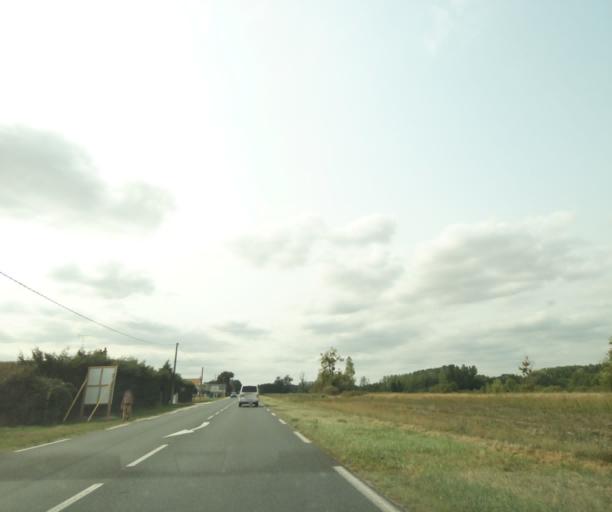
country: FR
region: Centre
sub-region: Departement de l'Indre
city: Chatillon-sur-Indre
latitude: 46.9977
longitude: 1.1547
